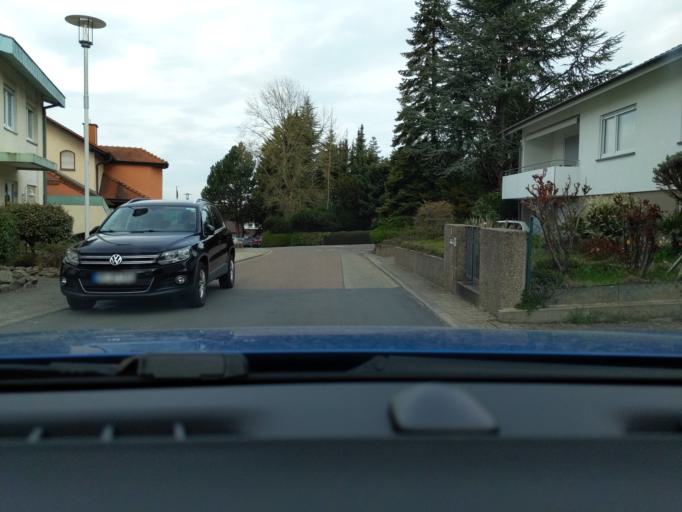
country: DE
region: Baden-Wuerttemberg
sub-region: Karlsruhe Region
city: Dielheim
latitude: 49.2869
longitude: 8.7373
